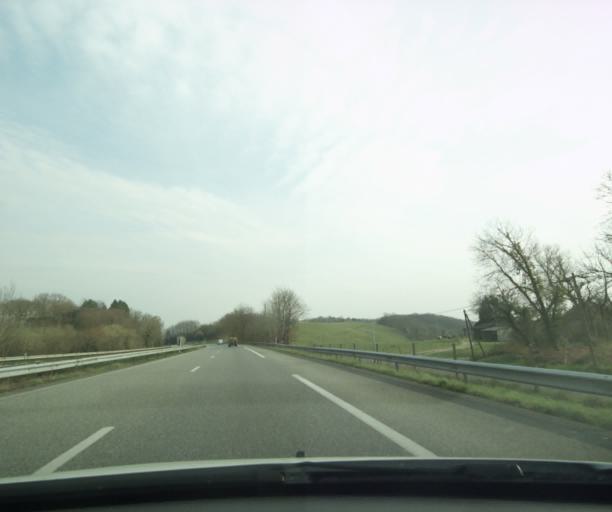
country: FR
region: Aquitaine
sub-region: Departement des Pyrenees-Atlantiques
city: Orthez
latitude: 43.4766
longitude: -0.7663
